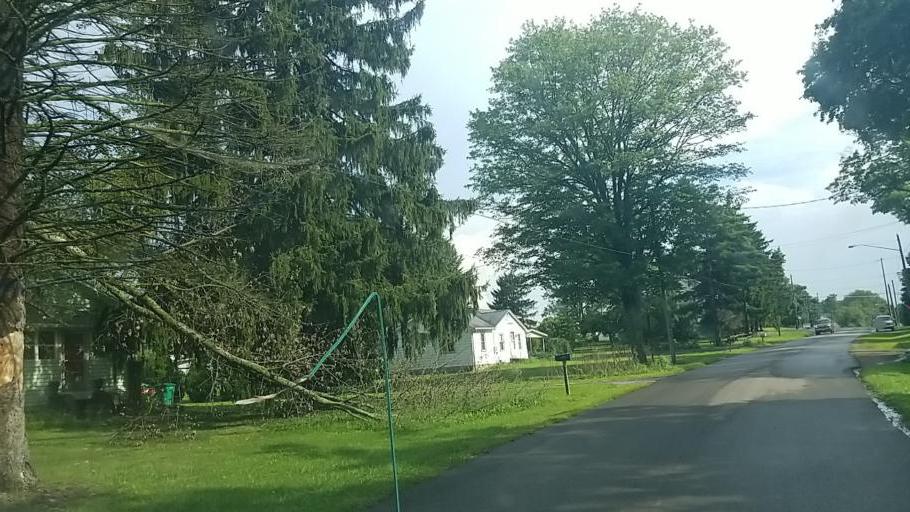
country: US
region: Ohio
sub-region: Wayne County
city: Creston
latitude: 40.9460
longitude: -81.9363
